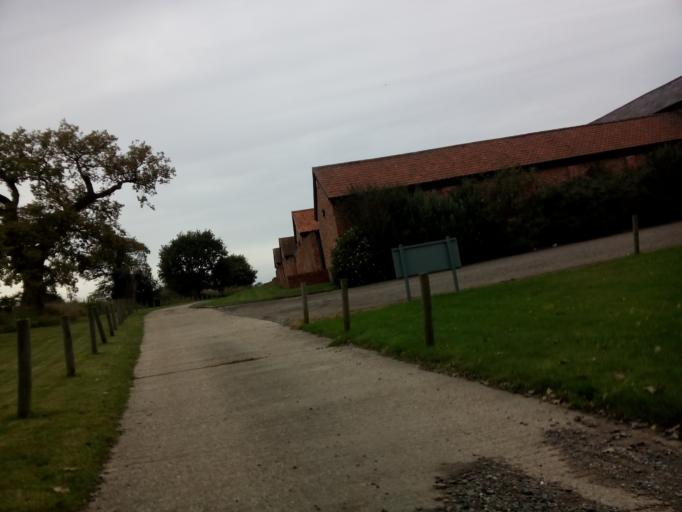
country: GB
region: England
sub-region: Suffolk
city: Ipswich
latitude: 52.0104
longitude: 1.1363
